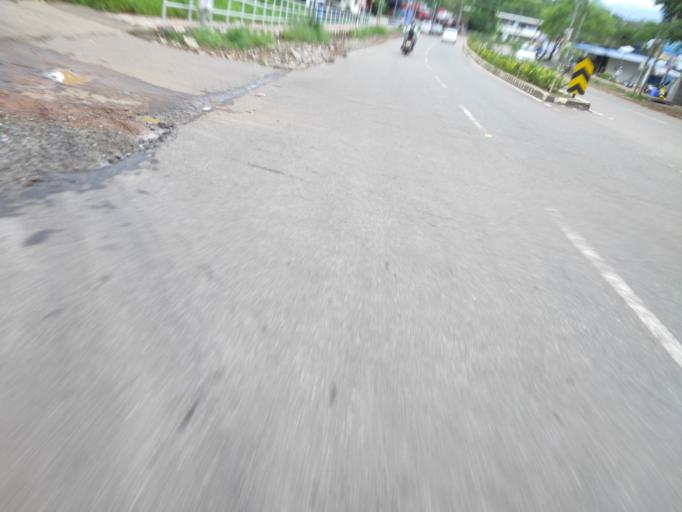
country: IN
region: Kerala
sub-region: Malappuram
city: Manjeri
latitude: 11.1974
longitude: 76.2292
